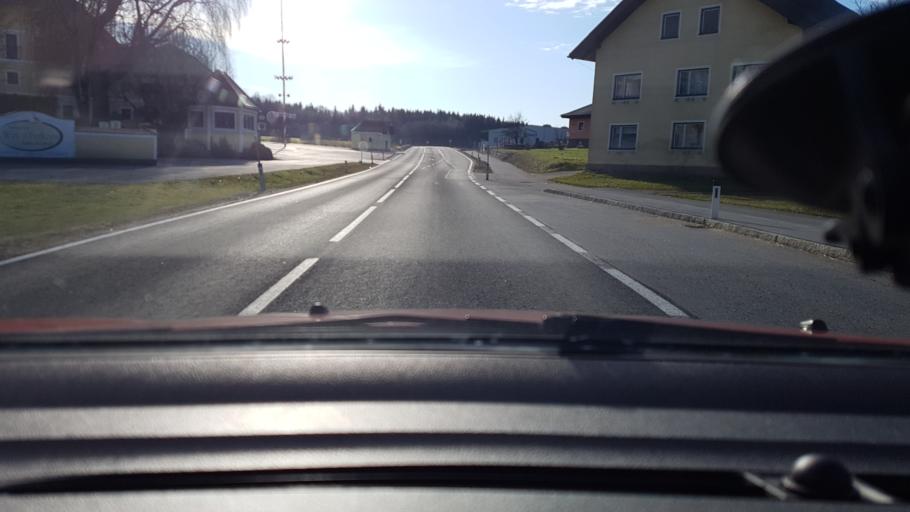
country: AT
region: Salzburg
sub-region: Politischer Bezirk Salzburg-Umgebung
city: Dorfbeuern
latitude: 48.0311
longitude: 12.9747
